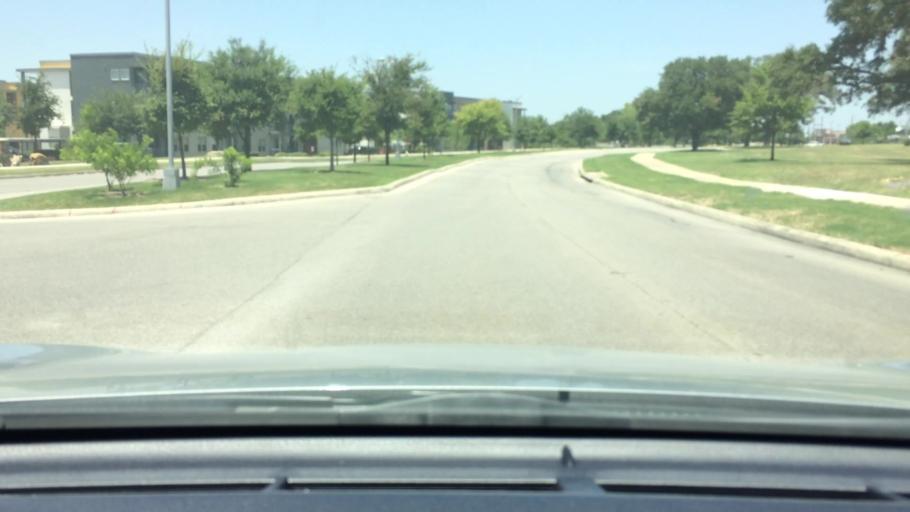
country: US
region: Texas
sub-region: Bexar County
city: San Antonio
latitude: 29.3483
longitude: -98.4473
